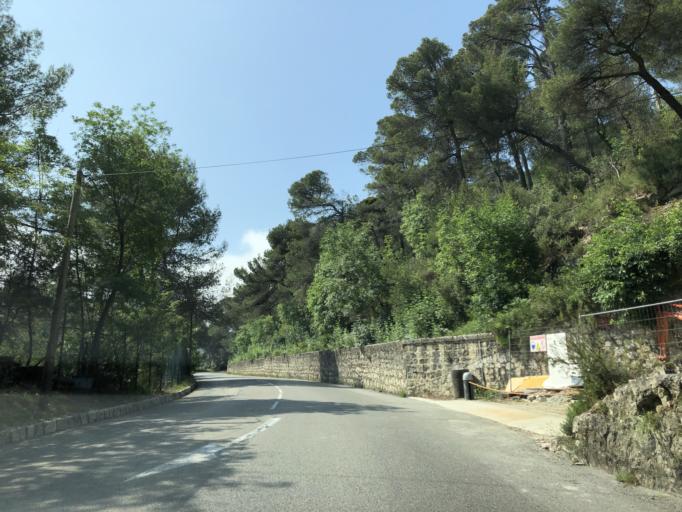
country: FR
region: Provence-Alpes-Cote d'Azur
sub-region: Departement des Alpes-Maritimes
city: La Trinite
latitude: 43.7284
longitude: 7.3028
